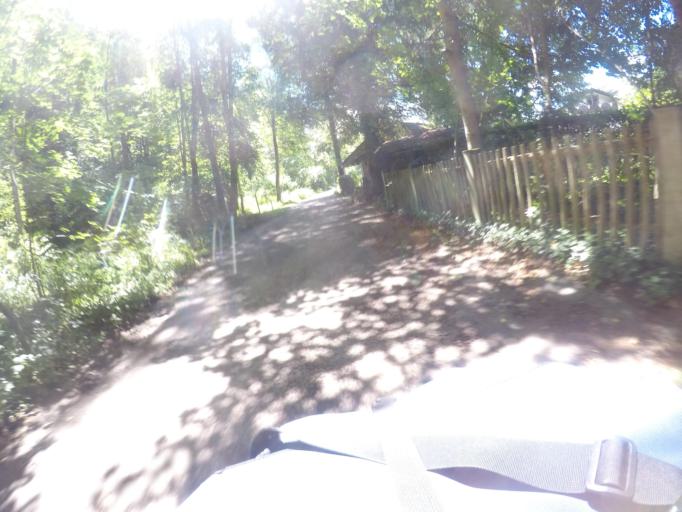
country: DE
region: Bavaria
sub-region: Swabia
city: Schwangau
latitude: 47.5593
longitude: 10.7475
